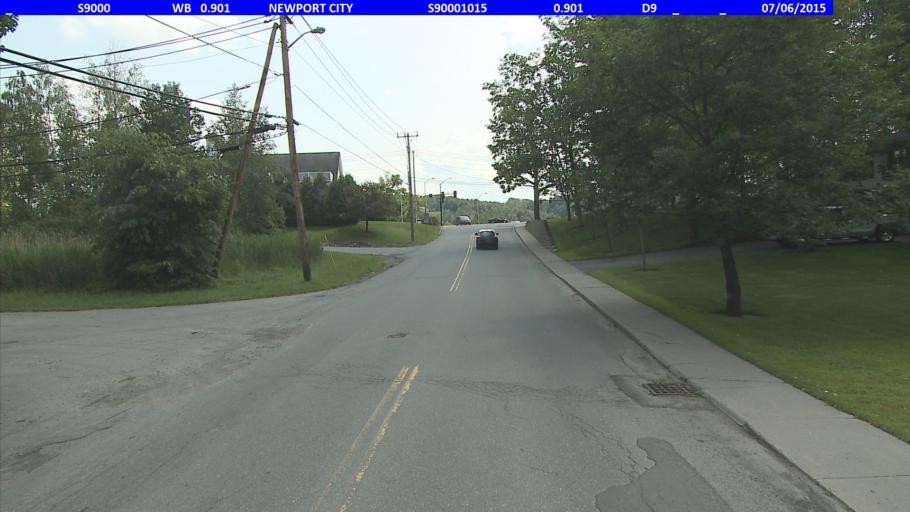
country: US
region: Vermont
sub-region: Orleans County
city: Newport
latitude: 44.9442
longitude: -72.1935
